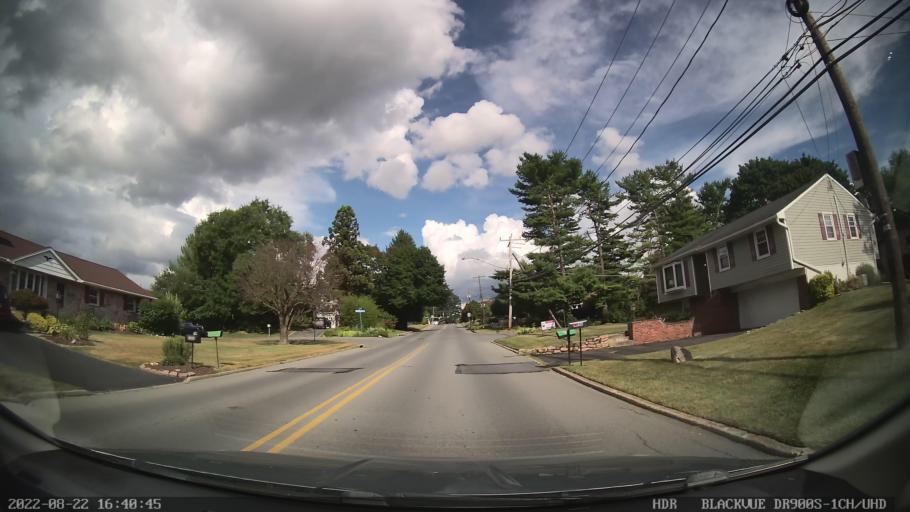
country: US
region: Pennsylvania
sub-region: Lehigh County
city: Dorneyville
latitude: 40.5708
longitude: -75.5222
